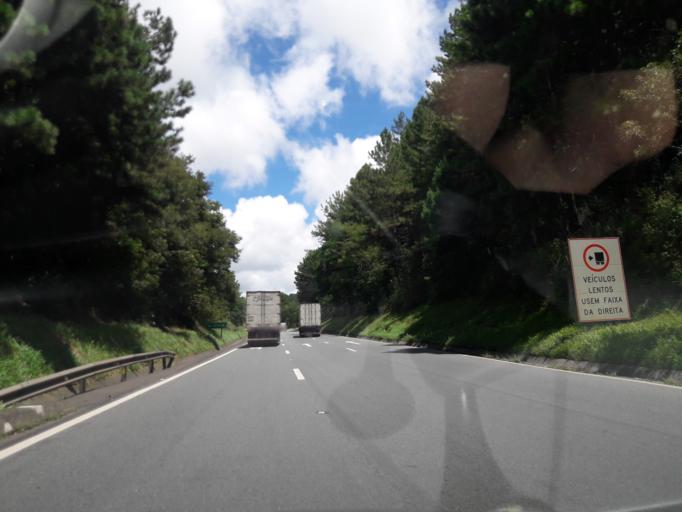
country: BR
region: Parana
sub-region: Campina Grande Do Sul
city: Campina Grande do Sul
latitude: -25.1820
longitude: -48.8829
